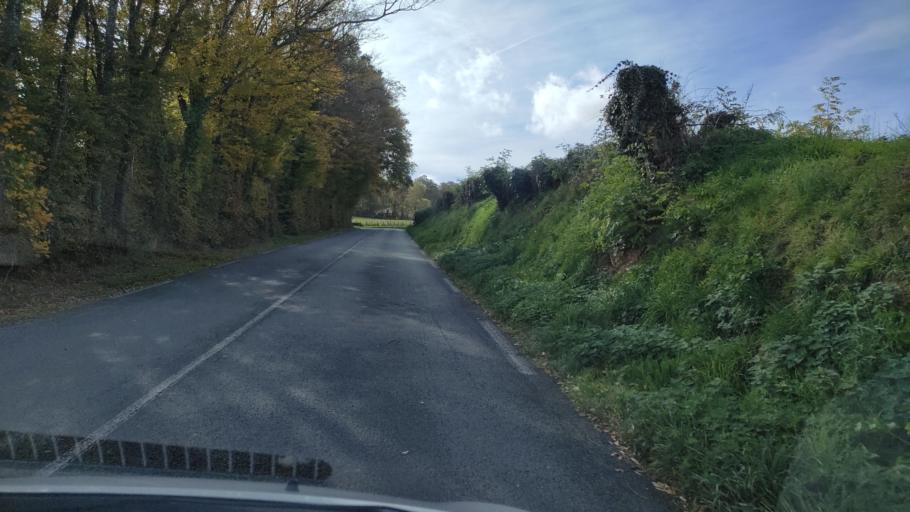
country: FR
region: Limousin
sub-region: Departement de la Haute-Vienne
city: Isle
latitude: 45.8148
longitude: 1.2147
